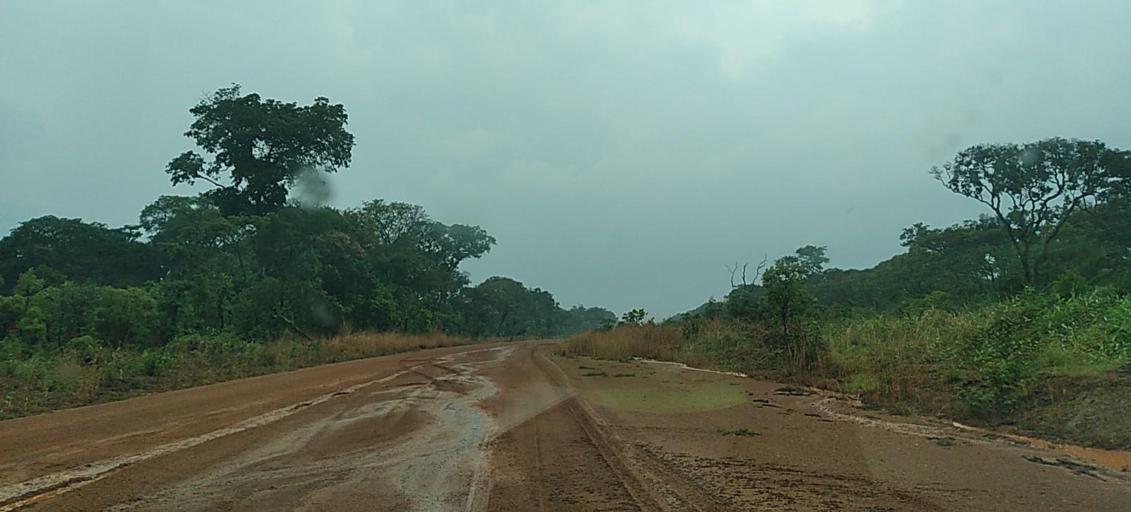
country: ZM
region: North-Western
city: Mwinilunga
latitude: -11.5986
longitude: 24.3924
